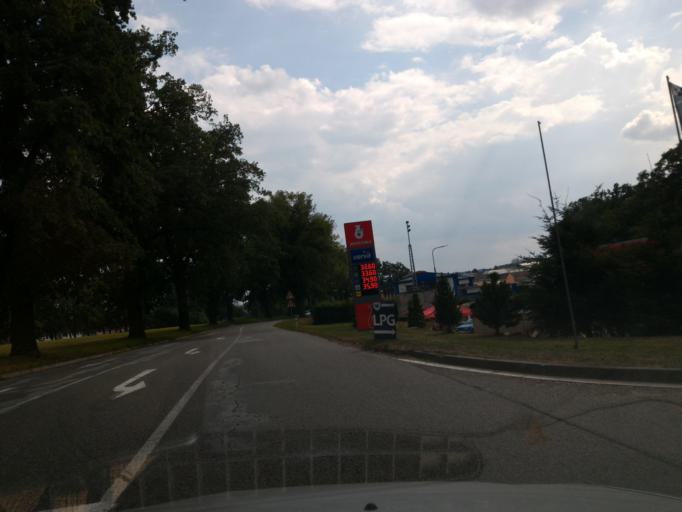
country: CZ
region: Vysocina
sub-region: Okres Jihlava
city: Trest'
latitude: 49.3009
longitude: 15.4829
